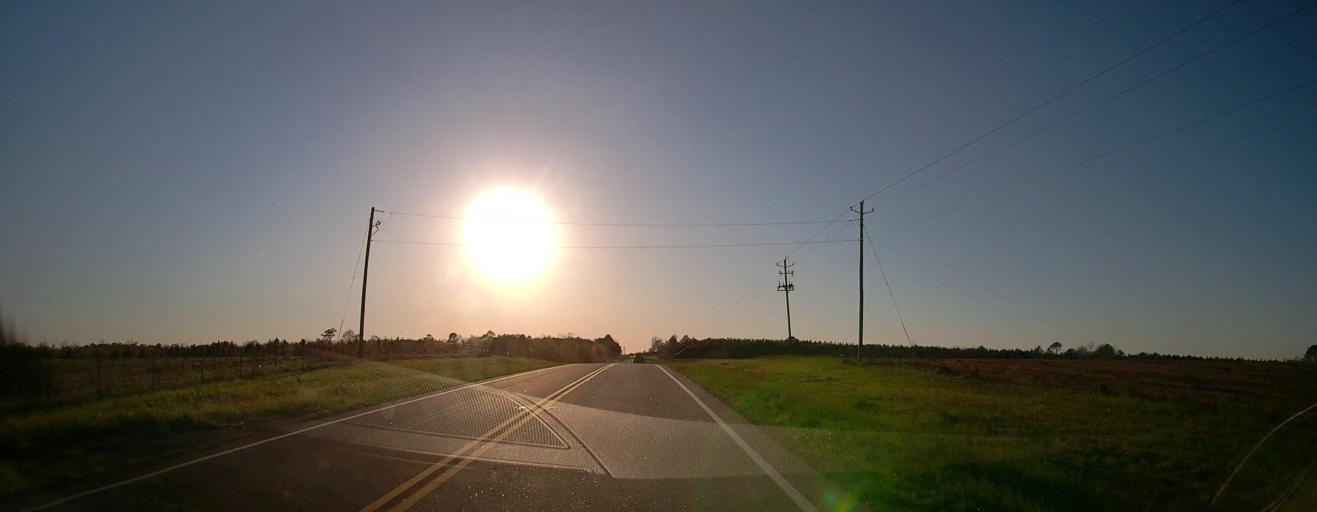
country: US
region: Georgia
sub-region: Wilcox County
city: Rochelle
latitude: 31.9610
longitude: -83.4150
